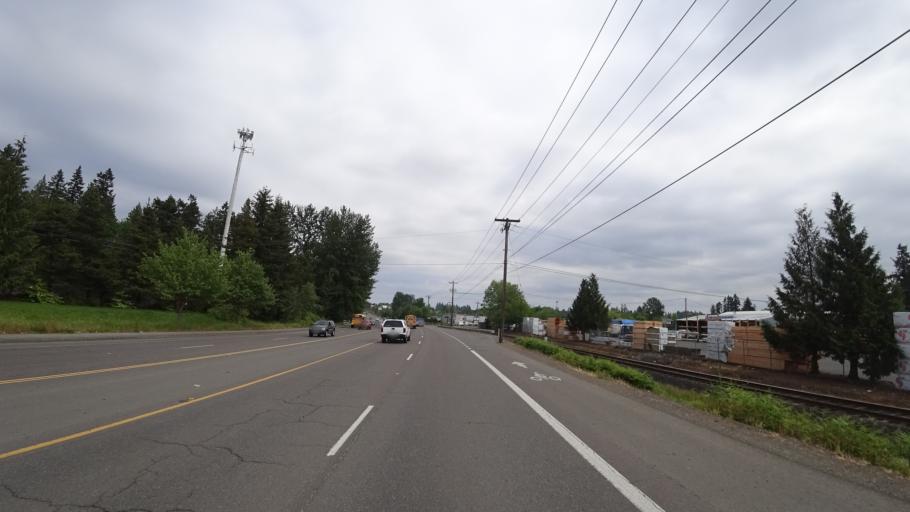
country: US
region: Oregon
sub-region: Washington County
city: Hillsboro
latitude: 45.5028
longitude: -122.9517
